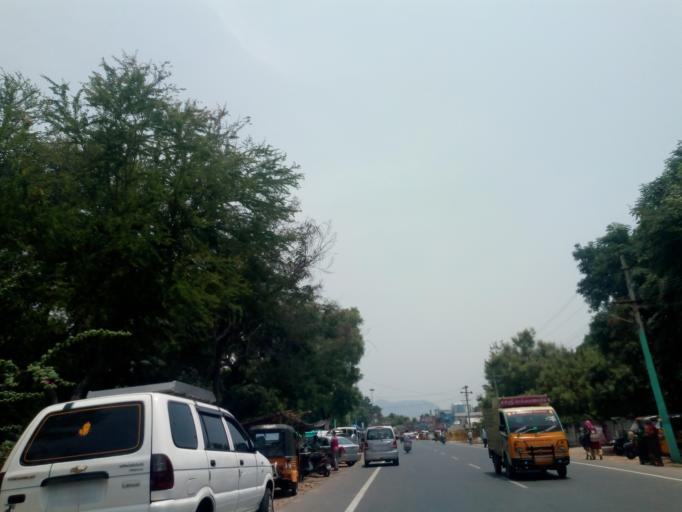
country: IN
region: Tamil Nadu
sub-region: Vellore
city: Vellore
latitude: 12.8701
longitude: 79.0896
